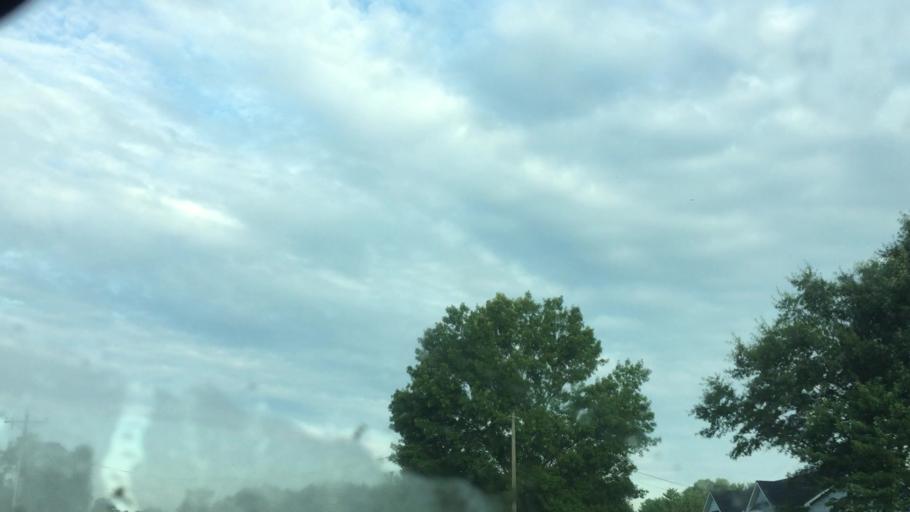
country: US
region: Georgia
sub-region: Henry County
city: McDonough
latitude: 33.5223
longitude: -84.1242
